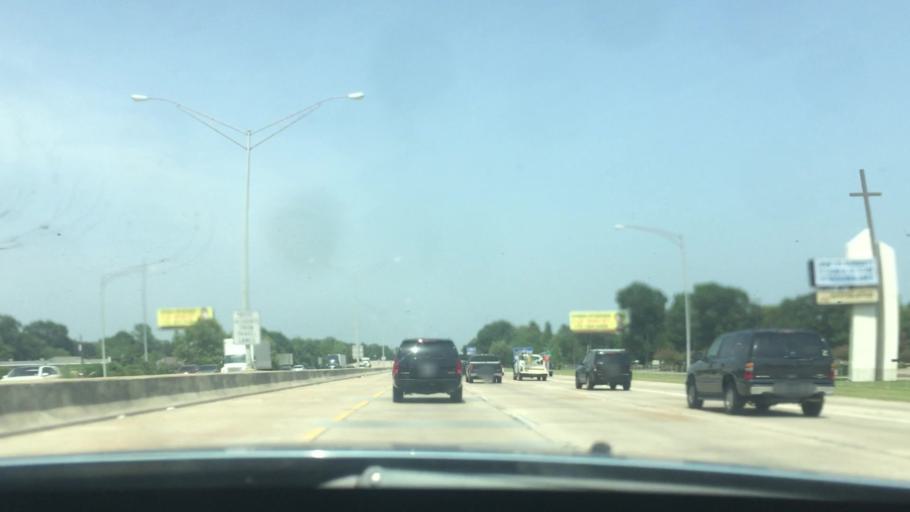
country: US
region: Louisiana
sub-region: East Baton Rouge Parish
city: Westminster
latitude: 30.4253
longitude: -91.0716
